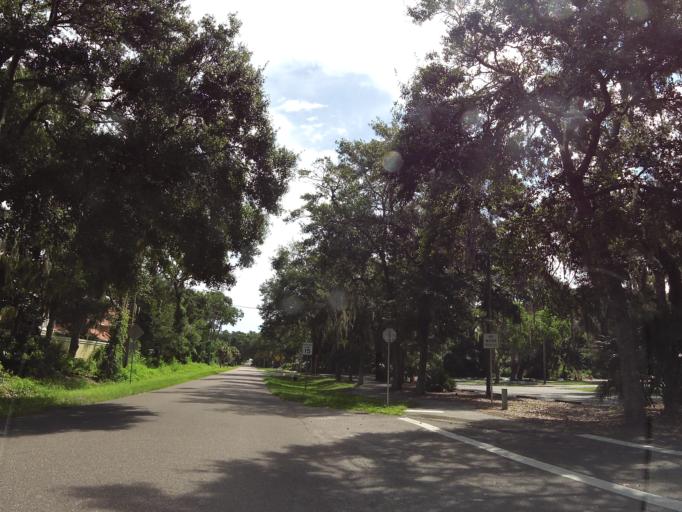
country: US
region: Florida
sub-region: Nassau County
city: Fernandina Beach
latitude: 30.5747
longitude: -81.4510
